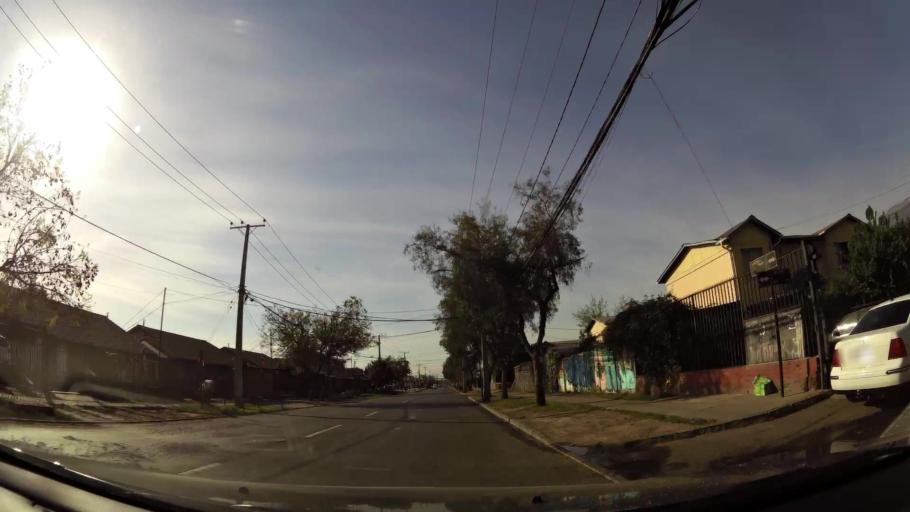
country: CL
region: Santiago Metropolitan
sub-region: Provincia de Cordillera
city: Puente Alto
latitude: -33.5846
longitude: -70.5582
